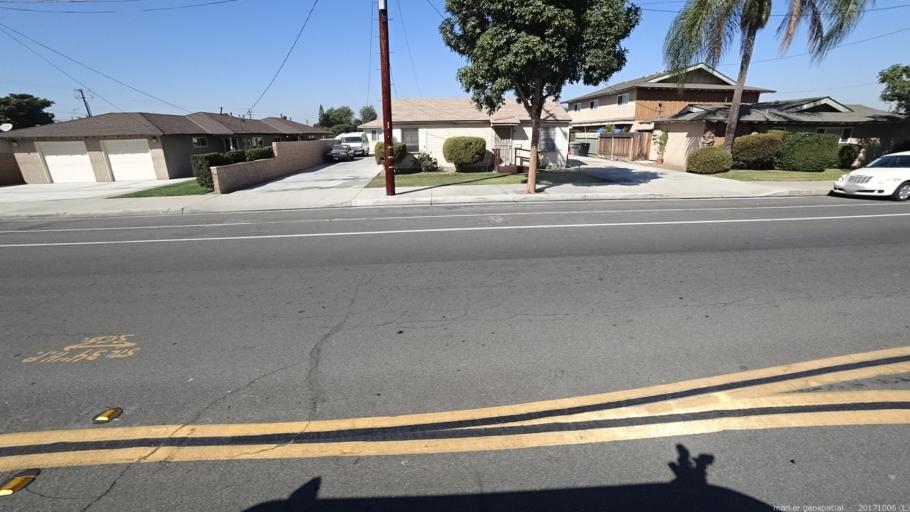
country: US
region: California
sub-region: Orange County
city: Garden Grove
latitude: 33.7814
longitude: -117.9448
